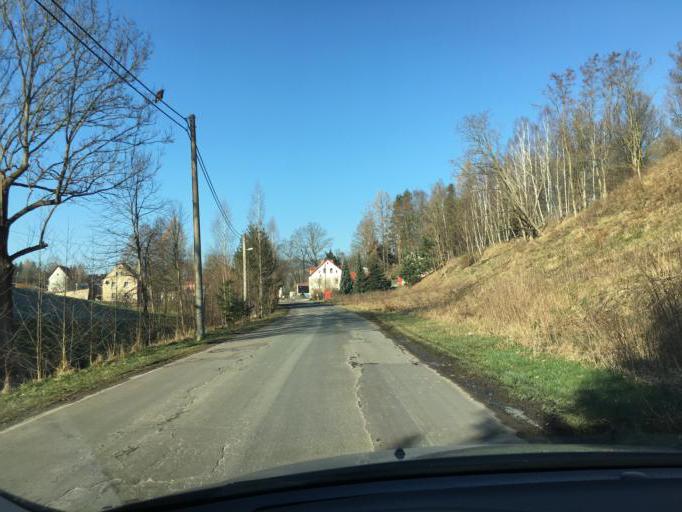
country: DE
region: Saxony
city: Lunzenau
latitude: 50.9634
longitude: 12.7374
